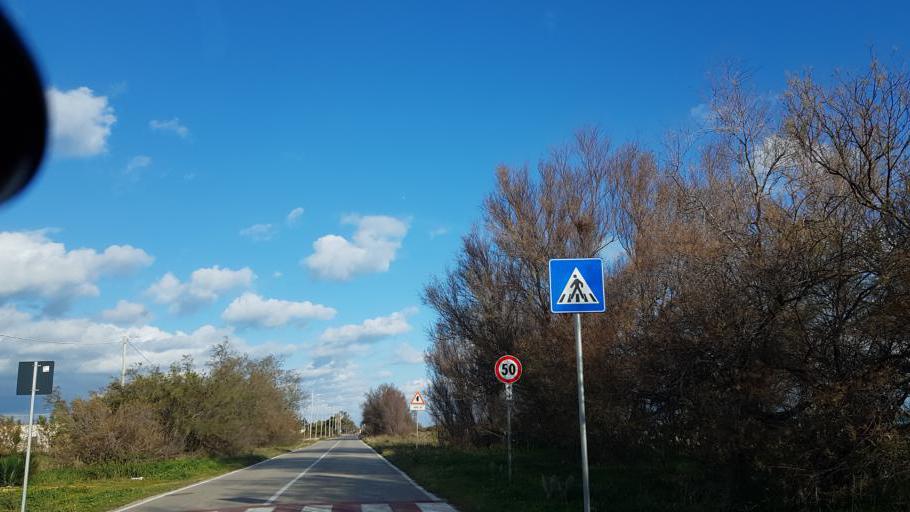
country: IT
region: Apulia
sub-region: Provincia di Brindisi
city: Materdomini
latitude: 40.6716
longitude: 17.9459
